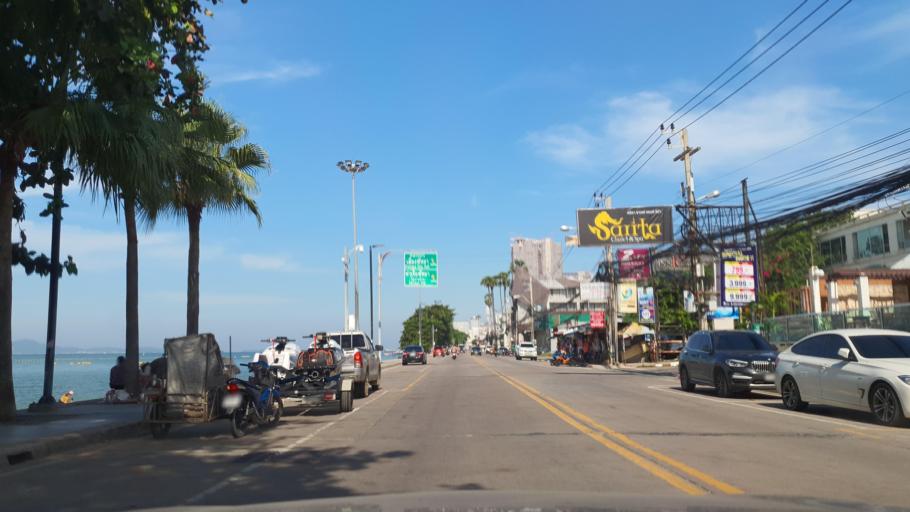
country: TH
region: Chon Buri
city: Phatthaya
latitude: 12.8818
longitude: 100.8816
